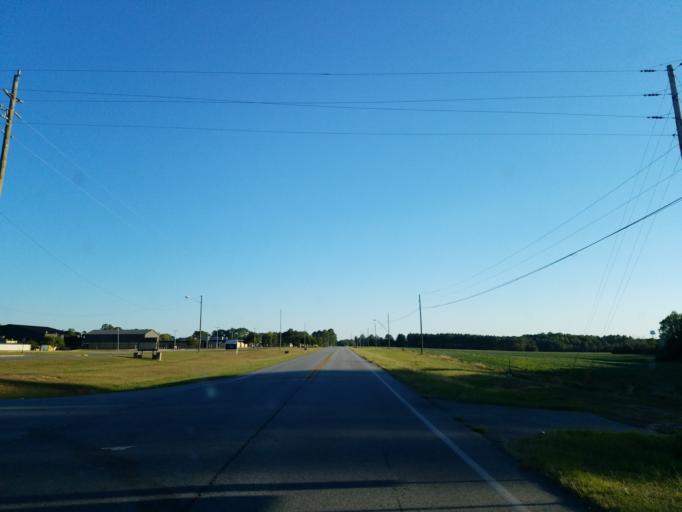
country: US
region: Georgia
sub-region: Worth County
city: Sylvester
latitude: 31.5511
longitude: -83.8430
